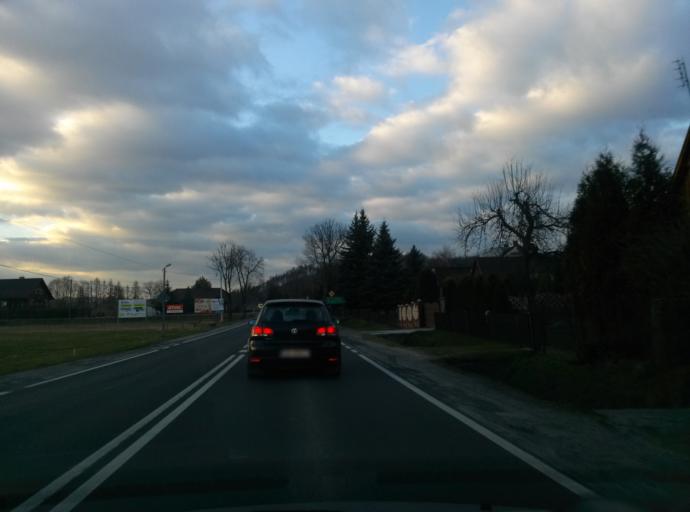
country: PL
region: Lesser Poland Voivodeship
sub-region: Powiat brzeski
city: Okocim
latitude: 49.9235
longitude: 20.5933
